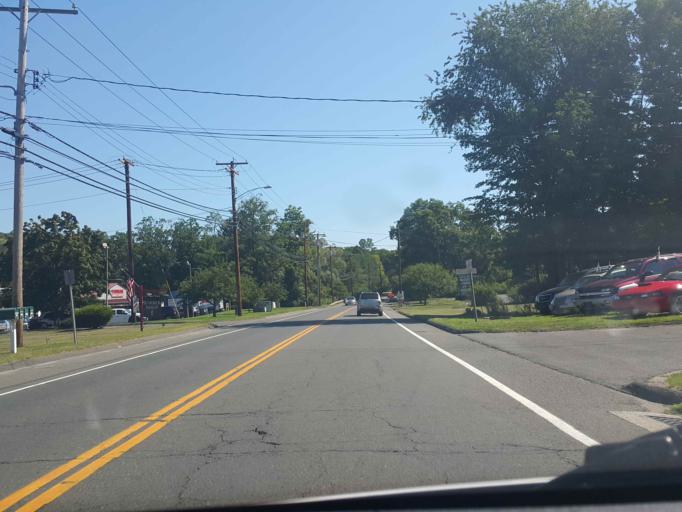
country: US
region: Connecticut
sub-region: New Haven County
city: North Branford
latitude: 41.3416
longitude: -72.7493
